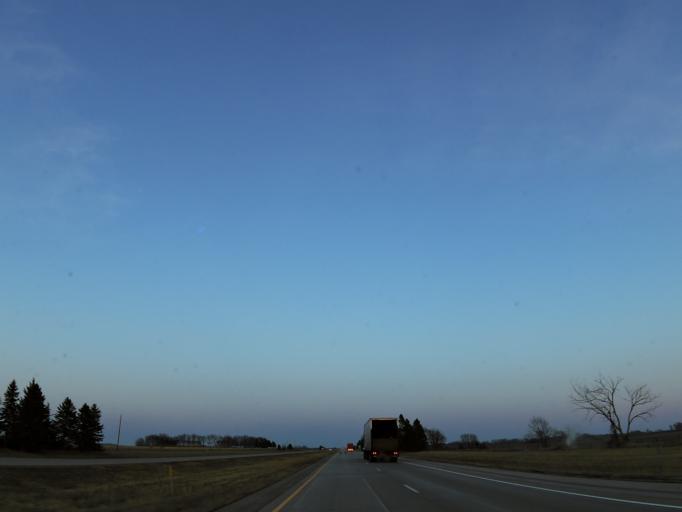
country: US
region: Minnesota
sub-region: Mower County
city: Austin
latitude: 43.6736
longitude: -92.8248
